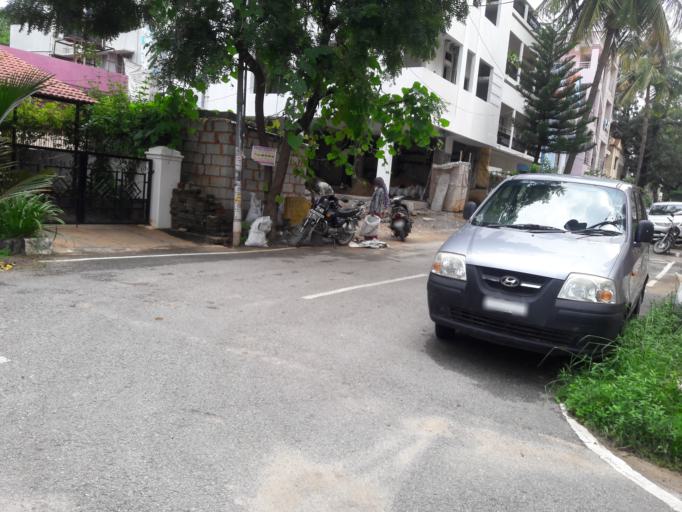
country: IN
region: Karnataka
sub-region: Bangalore Urban
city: Bangalore
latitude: 12.9823
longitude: 77.6481
